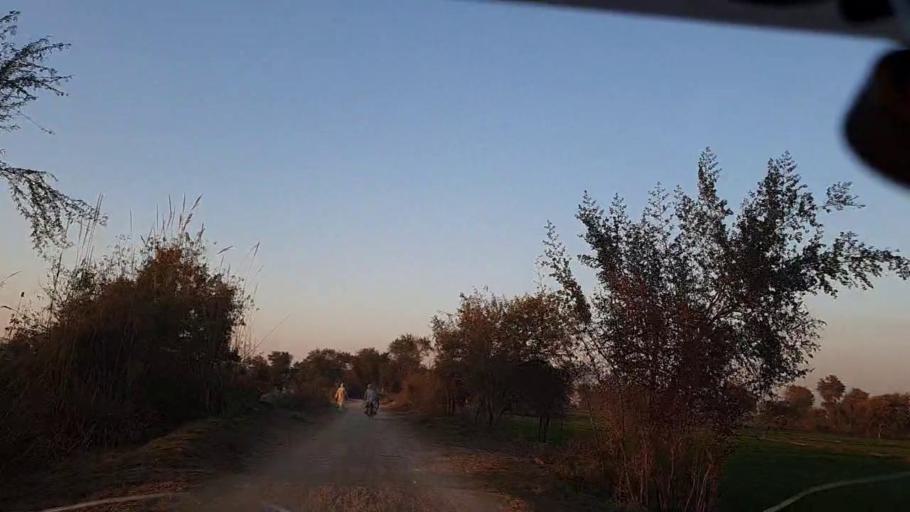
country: PK
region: Sindh
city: Adilpur
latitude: 27.8397
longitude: 69.2983
